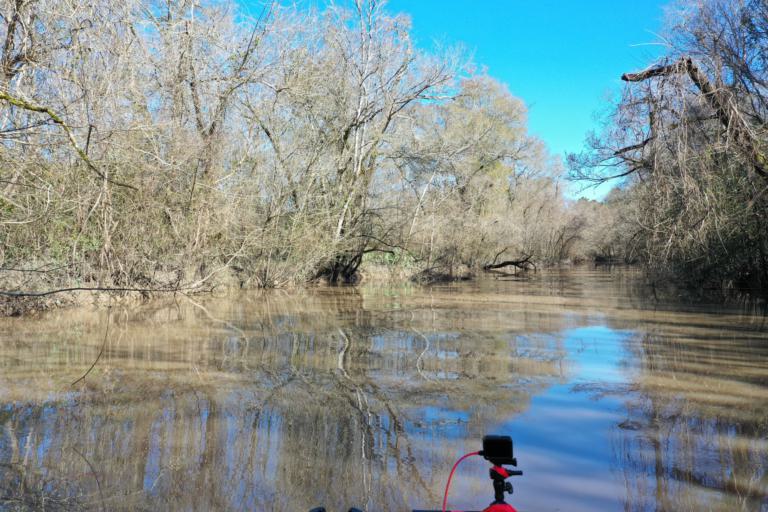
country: US
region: Louisiana
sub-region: Calcasieu Parish
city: Iowa
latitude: 30.3117
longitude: -93.0606
